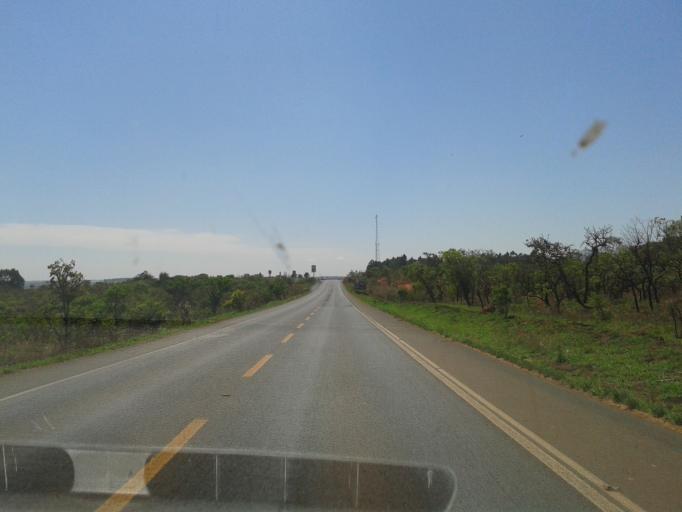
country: BR
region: Minas Gerais
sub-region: Sacramento
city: Sacramento
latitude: -19.3201
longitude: -47.5530
